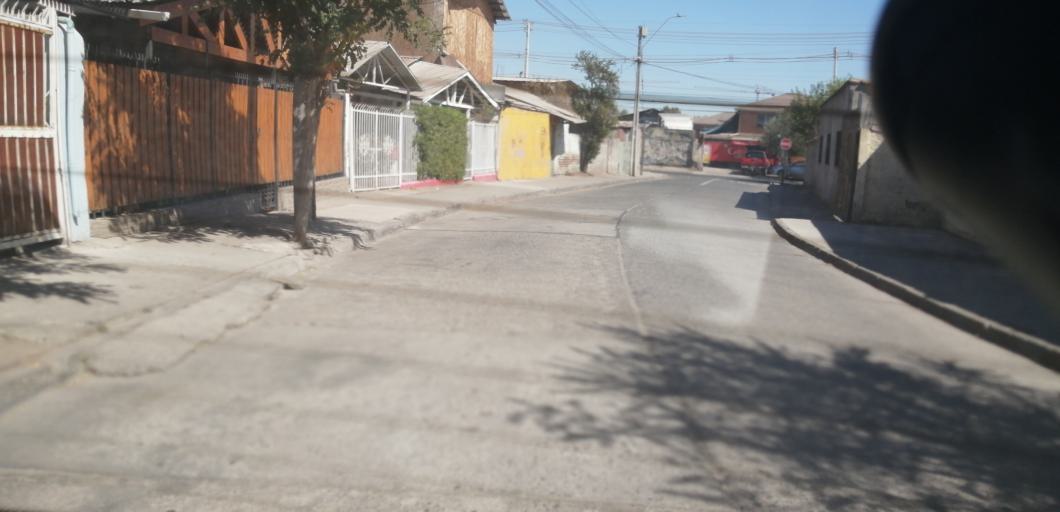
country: CL
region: Santiago Metropolitan
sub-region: Provincia de Santiago
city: Lo Prado
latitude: -33.4415
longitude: -70.7680
